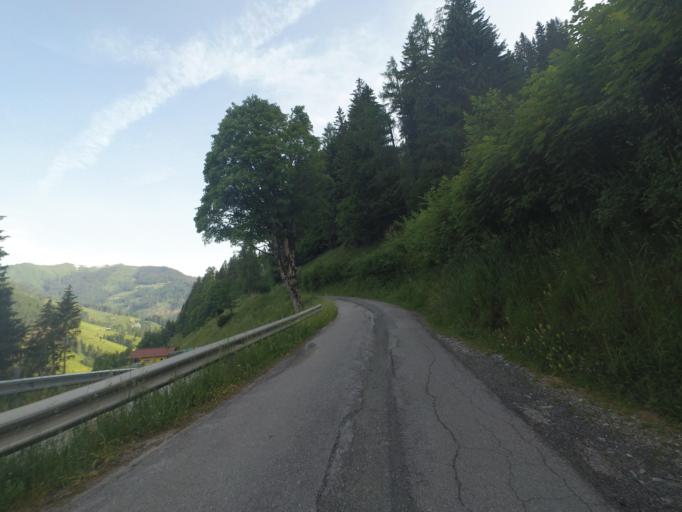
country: AT
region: Salzburg
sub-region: Politischer Bezirk Sankt Johann im Pongau
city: Muhlbach am Hochkonig
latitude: 47.3500
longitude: 13.1196
